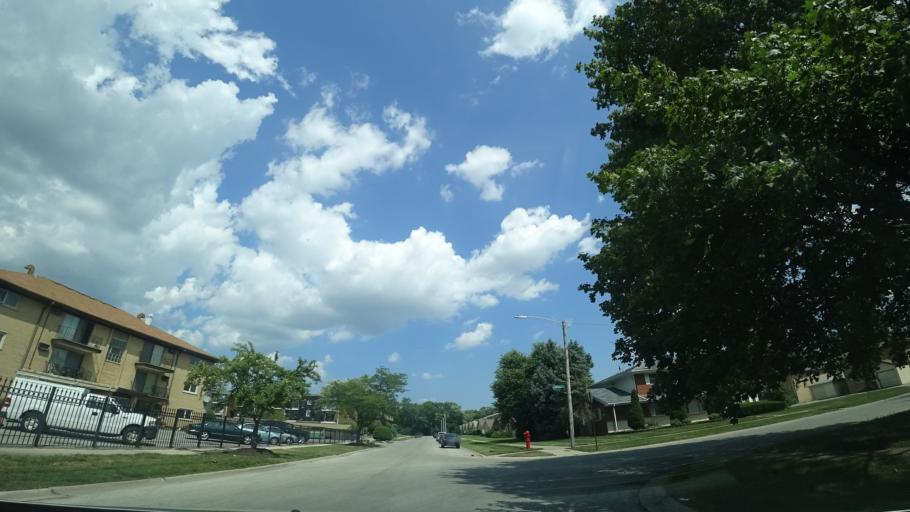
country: US
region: Illinois
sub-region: Cook County
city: Merrionette Park
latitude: 41.6751
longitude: -87.7127
